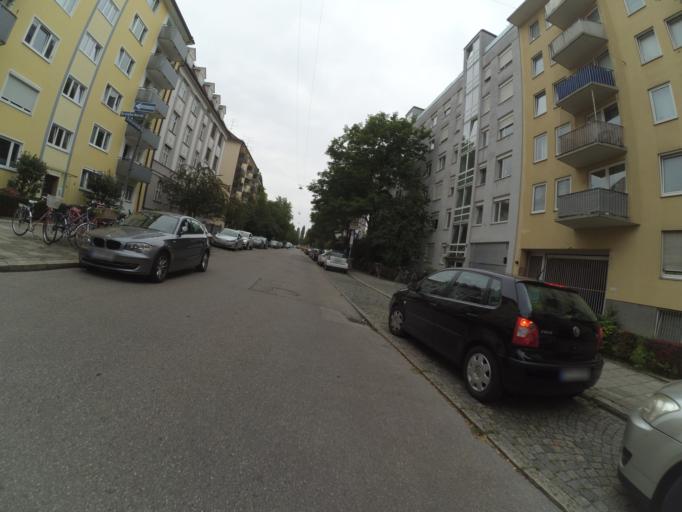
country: DE
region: Bavaria
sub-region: Upper Bavaria
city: Munich
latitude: 48.1592
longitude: 11.5648
